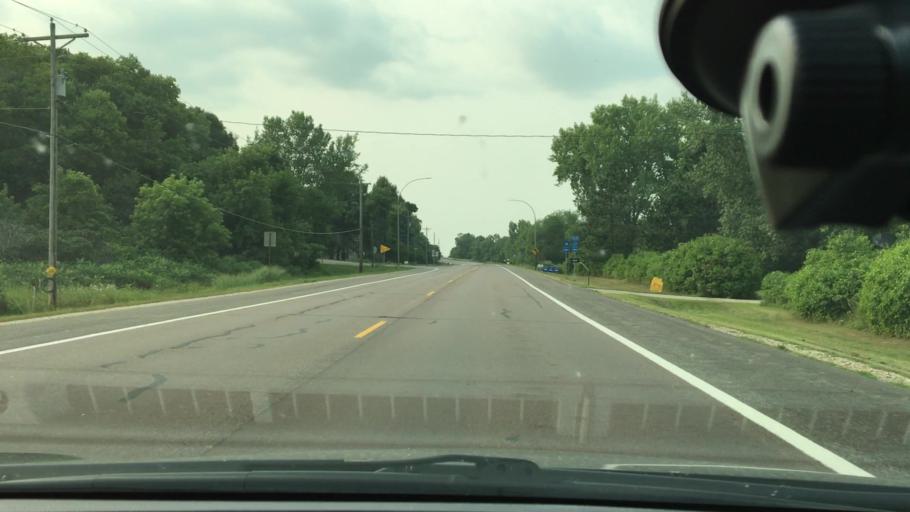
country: US
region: Minnesota
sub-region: Hennepin County
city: Dayton
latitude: 45.2513
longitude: -93.5369
